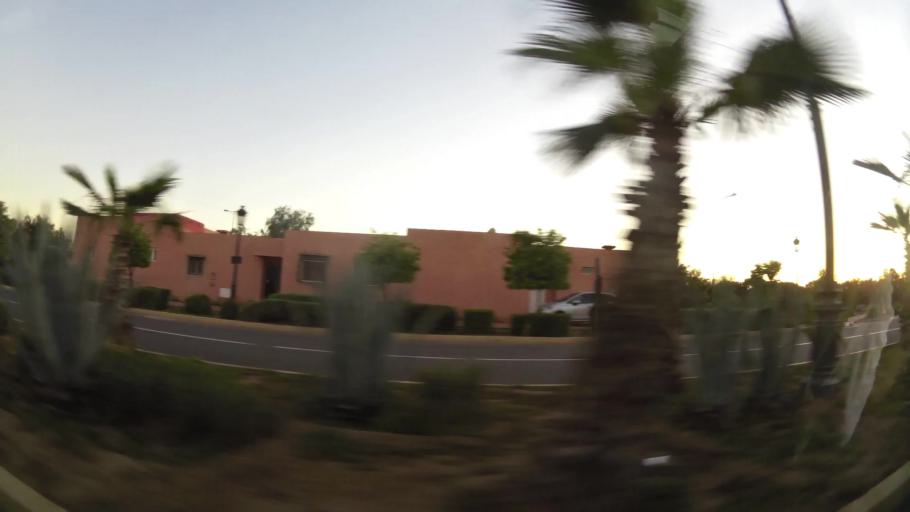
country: MA
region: Marrakech-Tensift-Al Haouz
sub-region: Kelaa-Des-Sraghna
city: Sidi Bou Othmane
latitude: 32.2164
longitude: -7.9310
